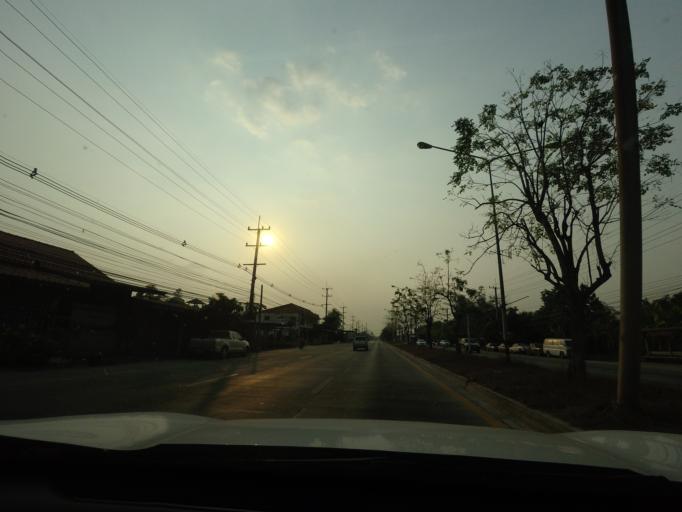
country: TH
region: Nakhon Nayok
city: Pak Phli
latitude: 14.1507
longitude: 101.3148
